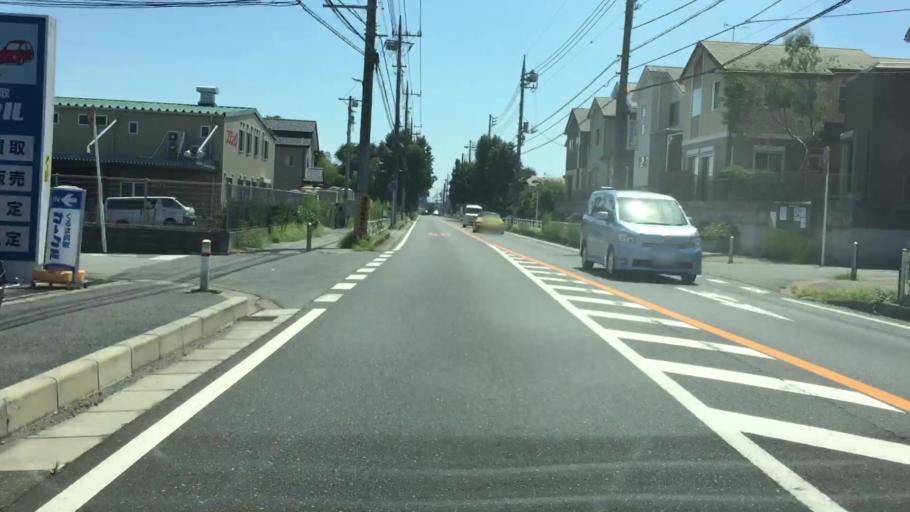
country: JP
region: Chiba
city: Matsudo
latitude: 35.7561
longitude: 139.9371
